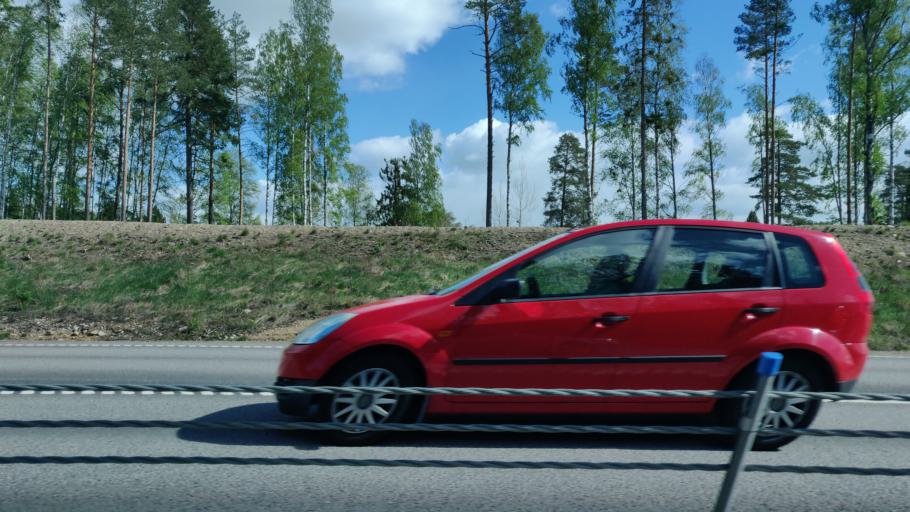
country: SE
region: Vaermland
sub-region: Karlstads Kommun
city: Karlstad
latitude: 59.4065
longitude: 13.5317
